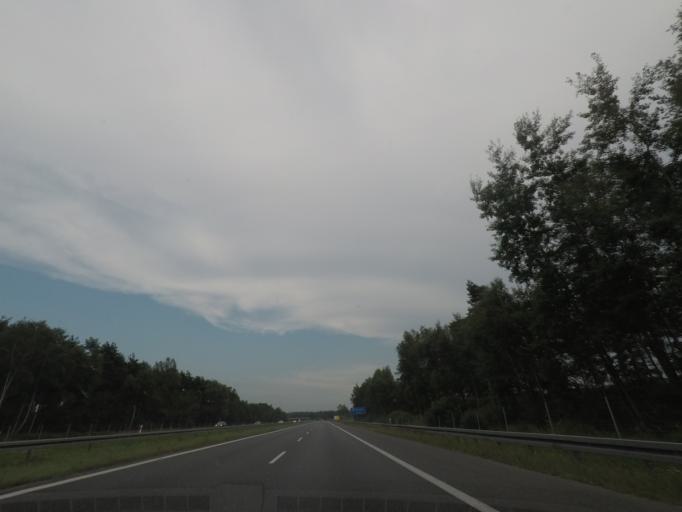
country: PL
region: Lesser Poland Voivodeship
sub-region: Powiat chrzanowski
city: Bolecin
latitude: 50.1147
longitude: 19.5036
